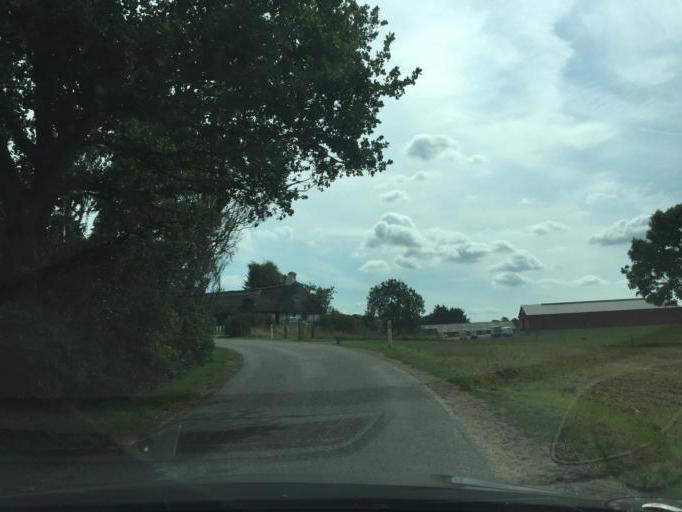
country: DK
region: South Denmark
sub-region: Assens Kommune
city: Tommerup Stationsby
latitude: 55.4042
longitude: 10.2340
